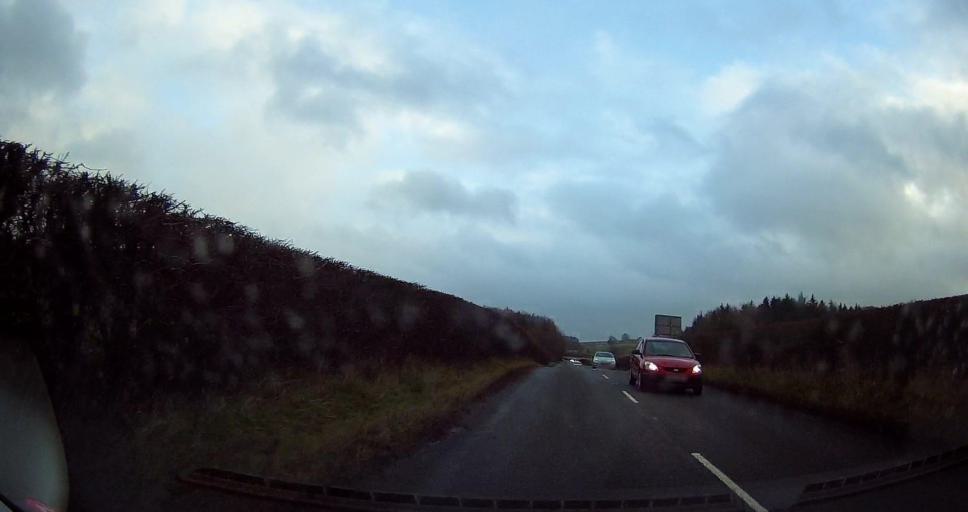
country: GB
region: England
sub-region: Derbyshire
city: Bakewell
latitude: 53.2322
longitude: -1.6721
